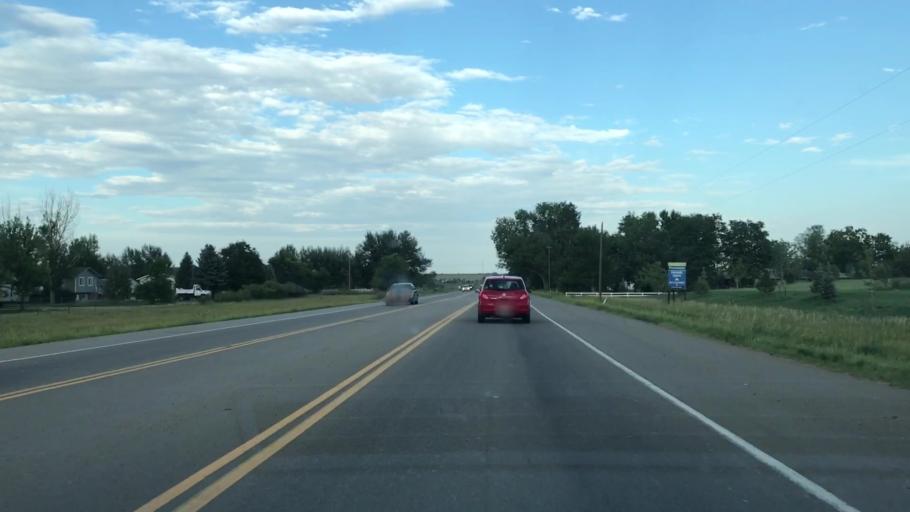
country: US
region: Colorado
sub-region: Boulder County
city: Longmont
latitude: 40.2035
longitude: -105.0621
